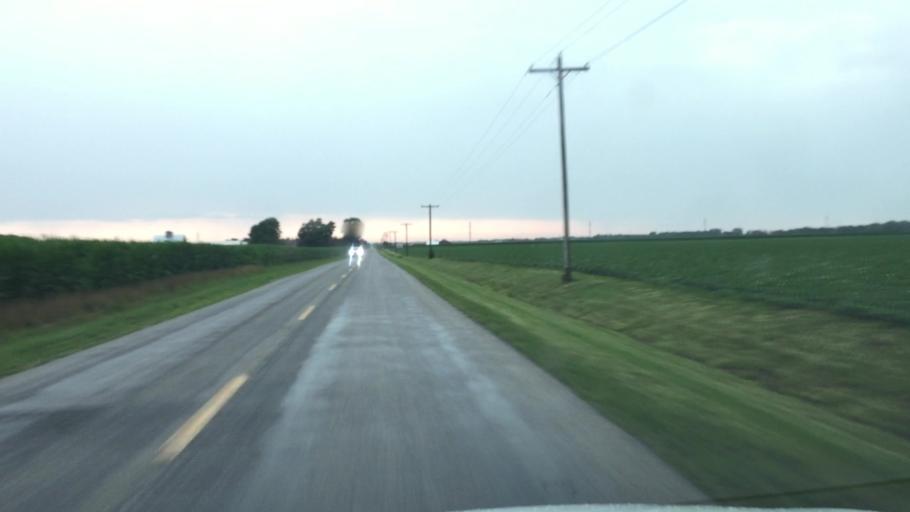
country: US
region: Iowa
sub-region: Lee County
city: Fort Madison
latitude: 40.5211
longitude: -91.2618
